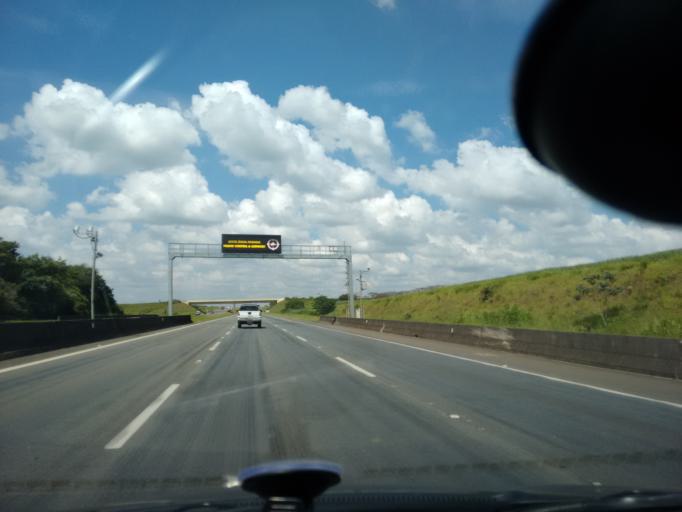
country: BR
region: Sao Paulo
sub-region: Santa Barbara D'Oeste
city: Santa Barbara d'Oeste
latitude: -22.7824
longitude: -47.4338
